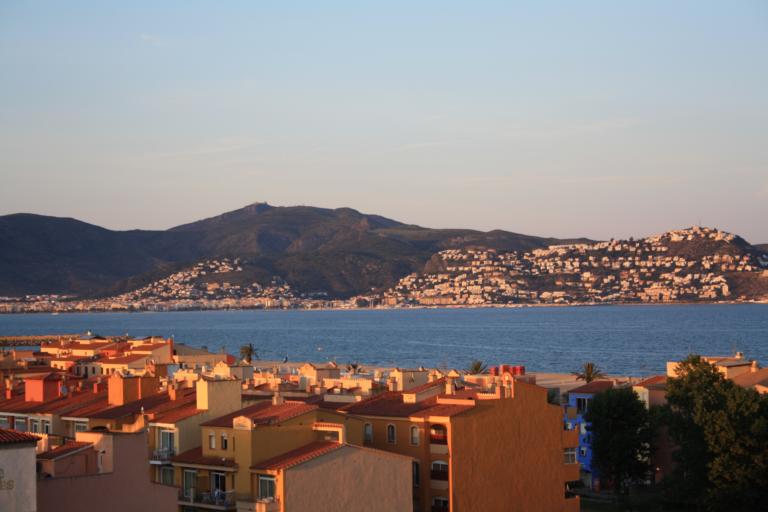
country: ES
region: Catalonia
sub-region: Provincia de Girona
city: Empuriabrava
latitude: 42.2402
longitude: 3.1234
